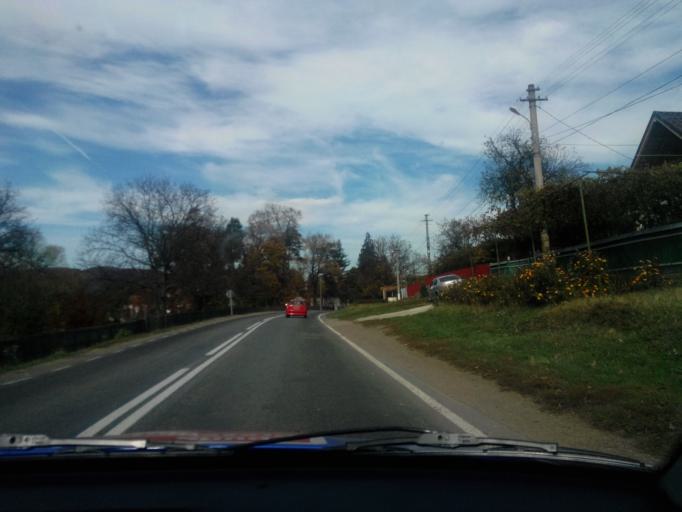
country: RO
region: Bacau
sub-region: Comuna Livezi
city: Livezi
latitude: 46.3932
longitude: 26.7307
